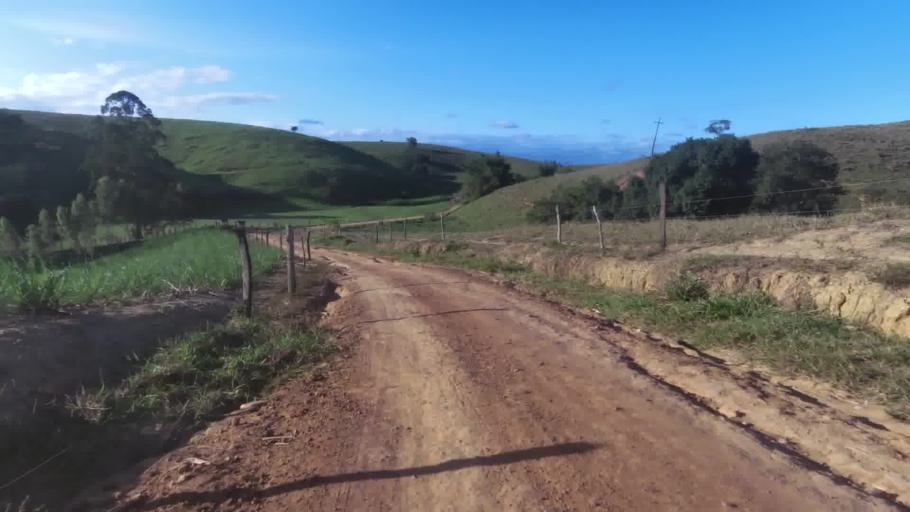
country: BR
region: Espirito Santo
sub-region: Marataizes
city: Marataizes
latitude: -21.1504
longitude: -41.0329
